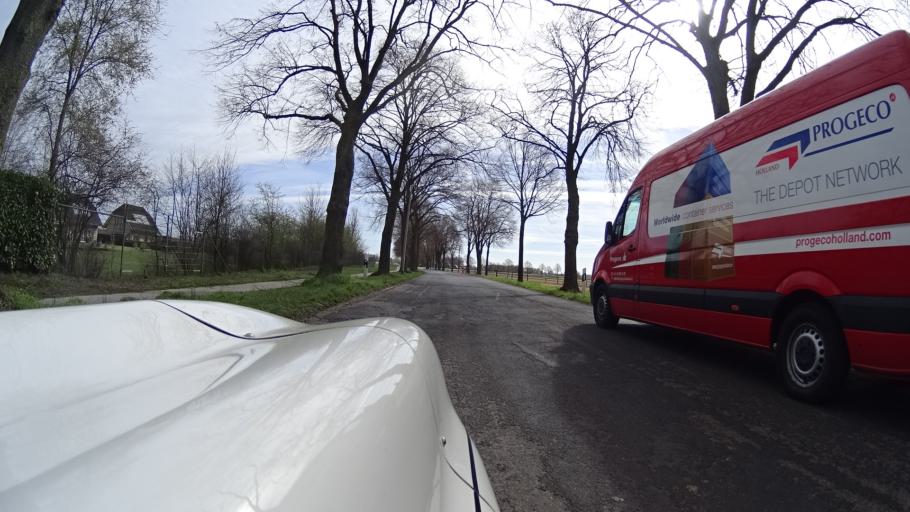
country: DE
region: North Rhine-Westphalia
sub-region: Regierungsbezirk Dusseldorf
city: Goch
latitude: 51.7043
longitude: 6.0814
